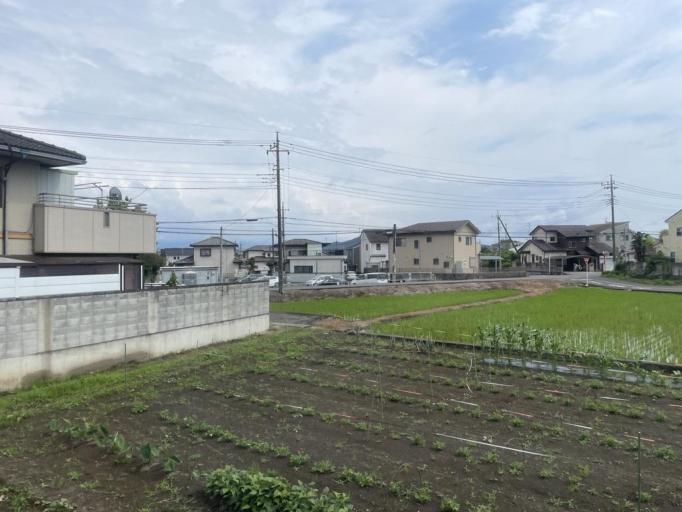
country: JP
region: Gunma
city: Kiryu
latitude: 36.4131
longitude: 139.3143
